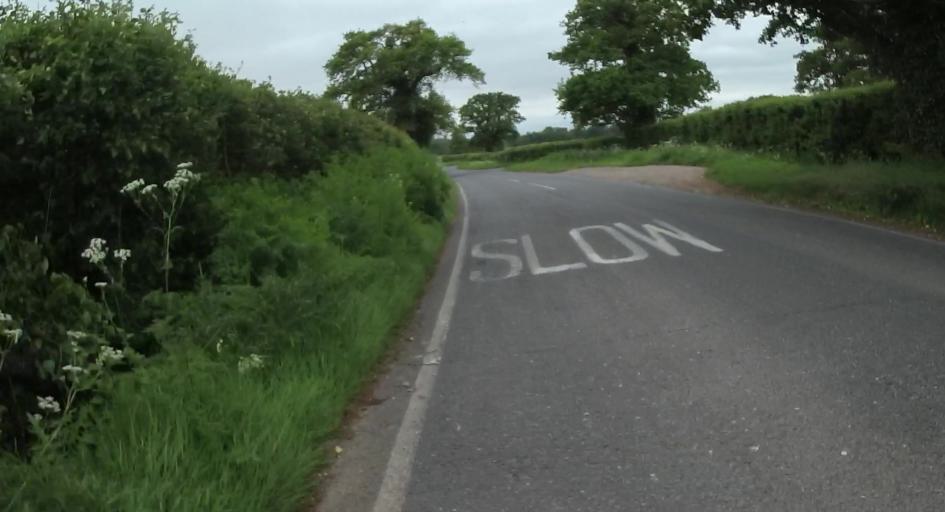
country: GB
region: England
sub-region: Wokingham
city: Swallowfield
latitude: 51.3772
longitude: -0.9343
